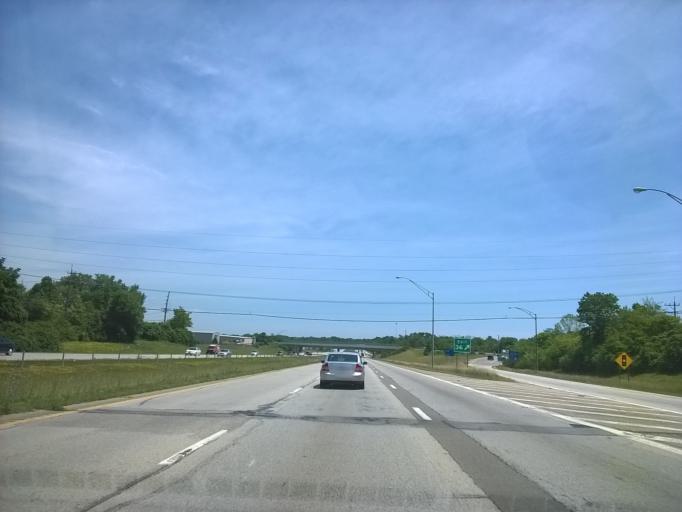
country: US
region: Ohio
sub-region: Hamilton County
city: Mount Healthy Heights
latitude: 39.2824
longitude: -84.5678
